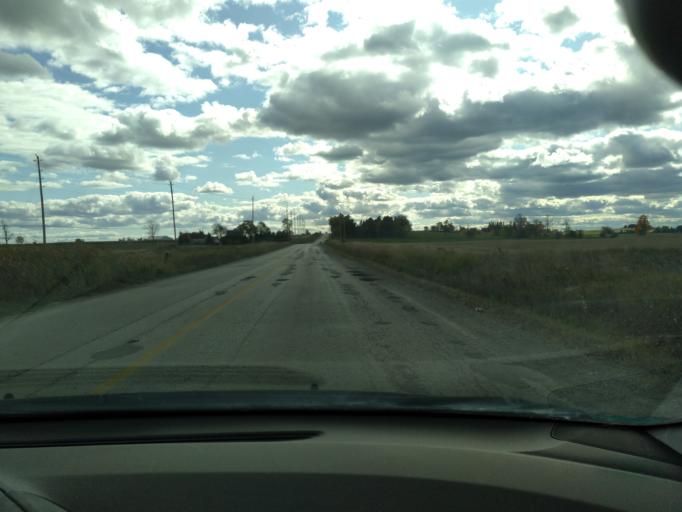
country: CA
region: Ontario
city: Bradford West Gwillimbury
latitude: 44.0918
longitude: -79.5982
